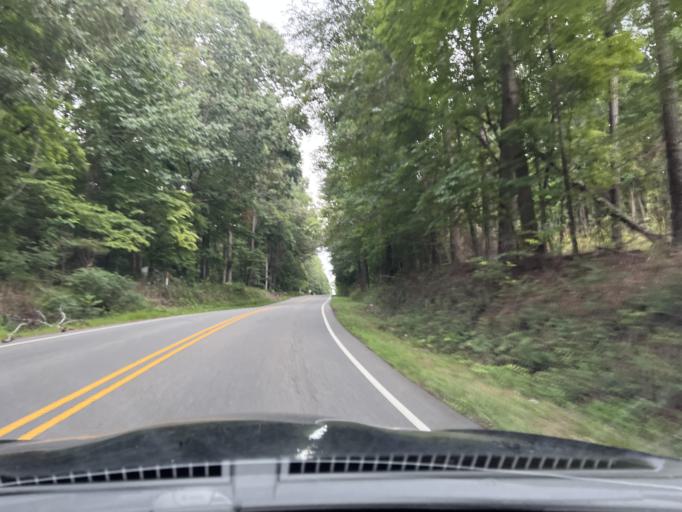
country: US
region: North Carolina
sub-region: Wake County
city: Wake Forest
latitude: 36.0070
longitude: -78.5275
